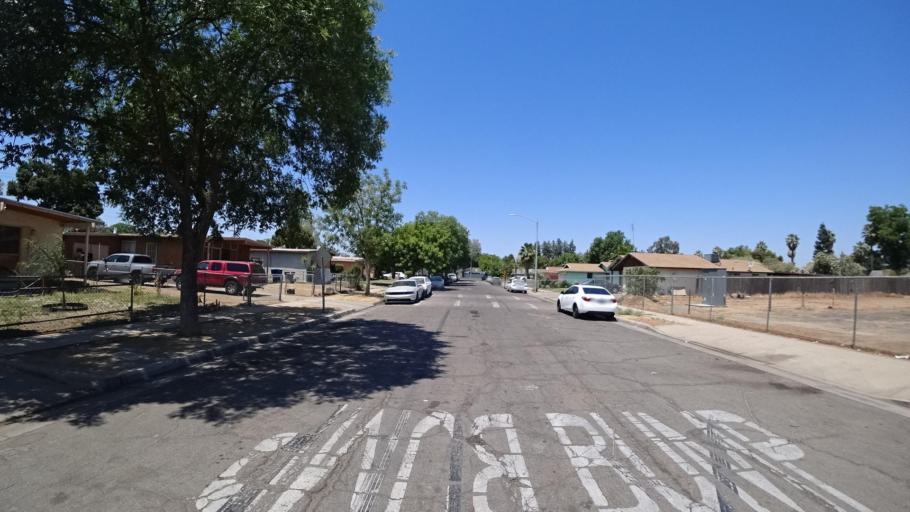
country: US
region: California
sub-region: Fresno County
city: West Park
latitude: 36.7274
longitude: -119.8160
